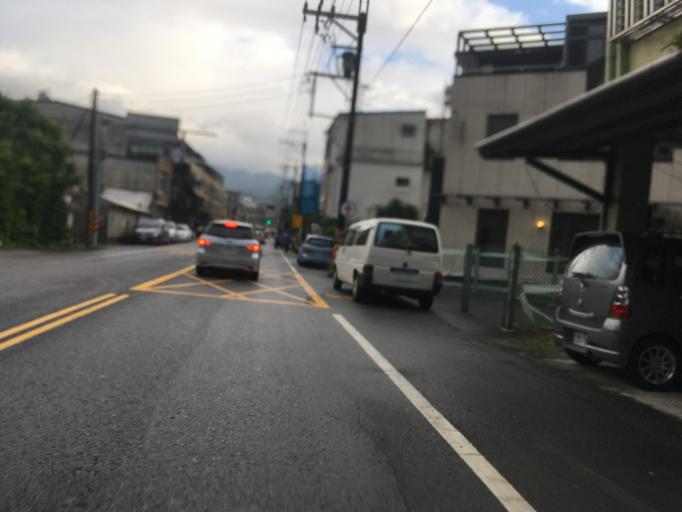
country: TW
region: Taiwan
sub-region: Yilan
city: Yilan
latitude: 24.8434
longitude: 121.8072
